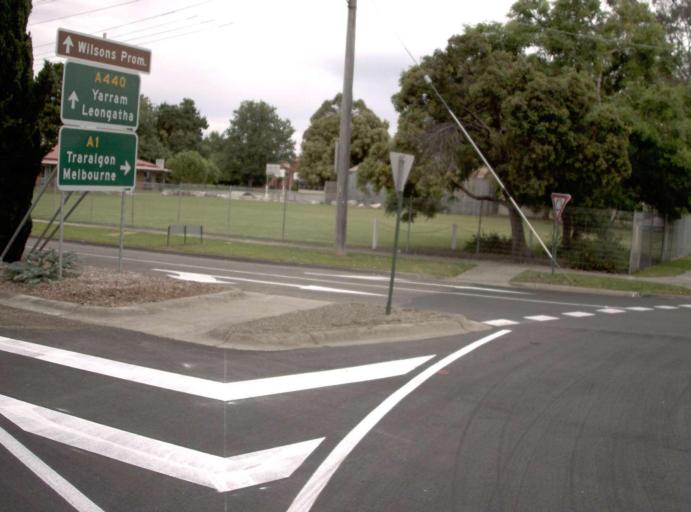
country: AU
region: Victoria
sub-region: Wellington
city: Sale
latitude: -38.1115
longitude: 147.0685
